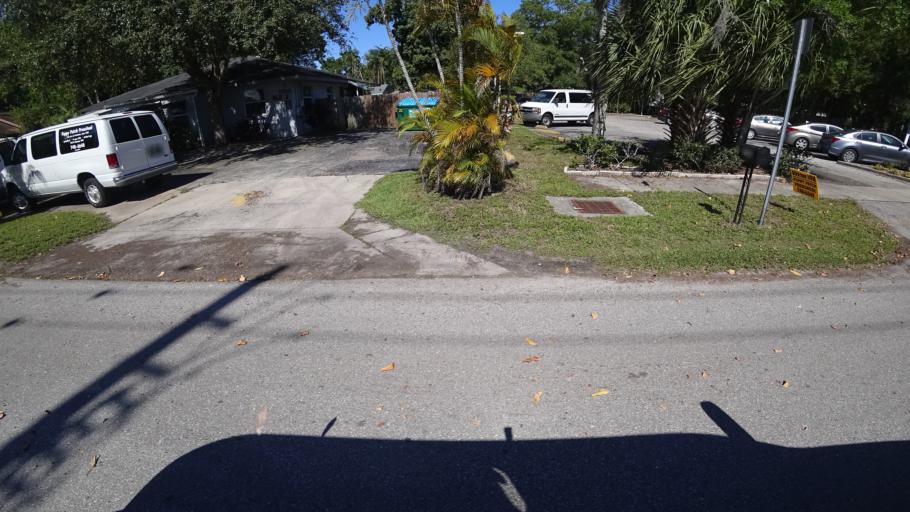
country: US
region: Florida
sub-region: Manatee County
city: West Bradenton
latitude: 27.4895
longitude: -82.5962
